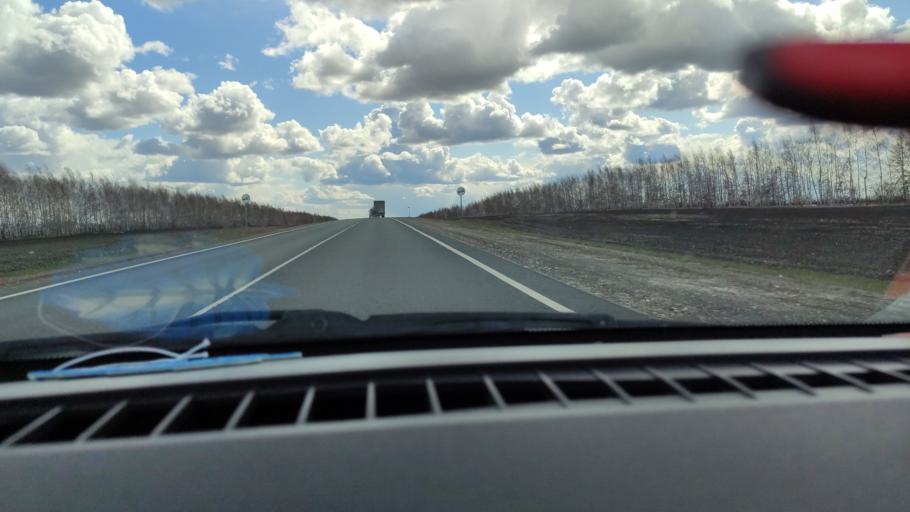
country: RU
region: Samara
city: Syzran'
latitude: 52.9072
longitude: 48.2984
